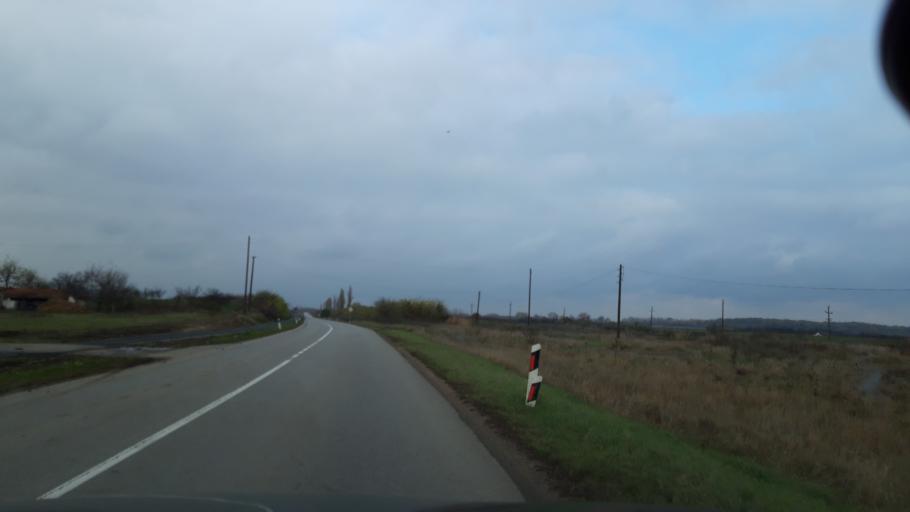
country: RS
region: Autonomna Pokrajina Vojvodina
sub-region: Severnobanatski Okrug
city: Novi Knezevac
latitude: 46.0637
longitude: 20.1033
